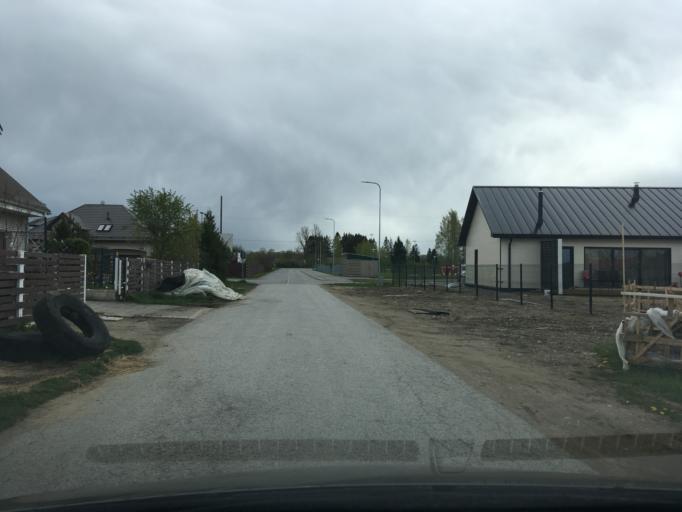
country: EE
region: Harju
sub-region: Joelaehtme vald
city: Loo
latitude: 59.4032
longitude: 24.9469
